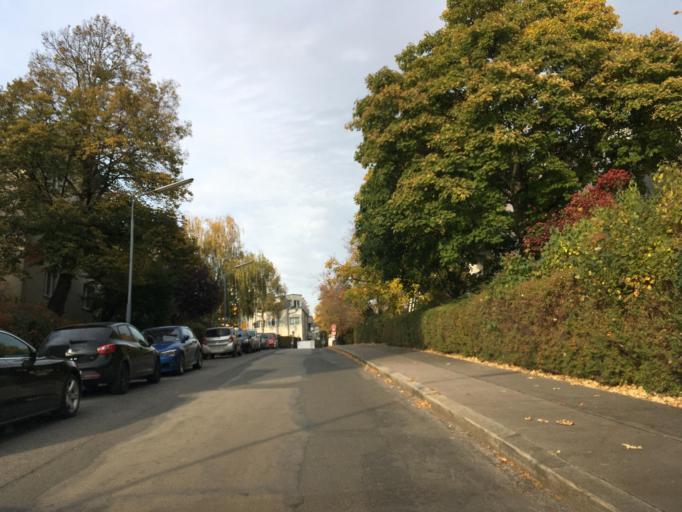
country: AT
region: Vienna
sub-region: Wien Stadt
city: Vienna
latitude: 48.2438
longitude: 16.3290
